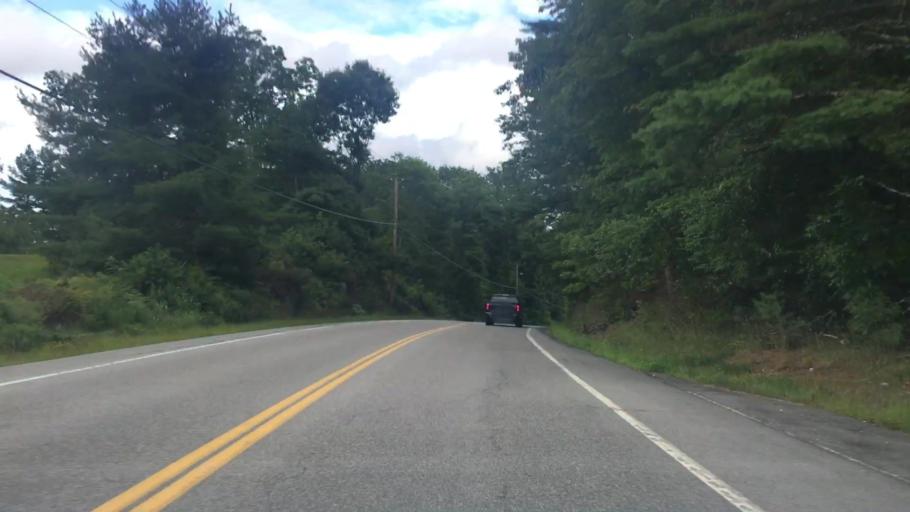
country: US
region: Maine
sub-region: York County
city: Dayton
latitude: 43.5427
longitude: -70.5207
